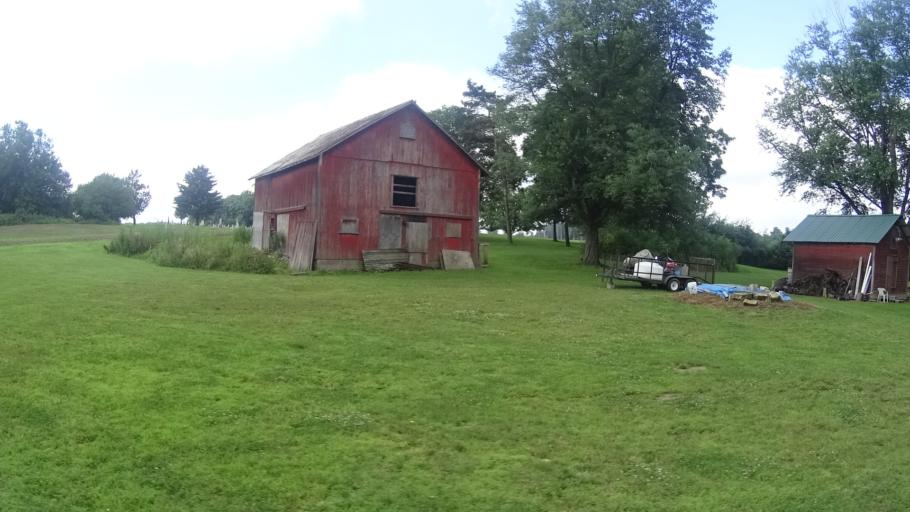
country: US
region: Ohio
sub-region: Huron County
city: Wakeman
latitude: 41.3106
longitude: -82.4423
